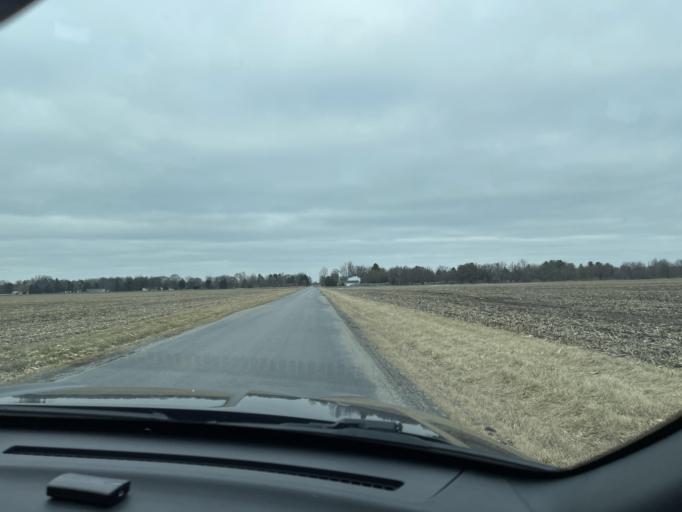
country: US
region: Illinois
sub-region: Sangamon County
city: Jerome
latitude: 39.7784
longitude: -89.7534
